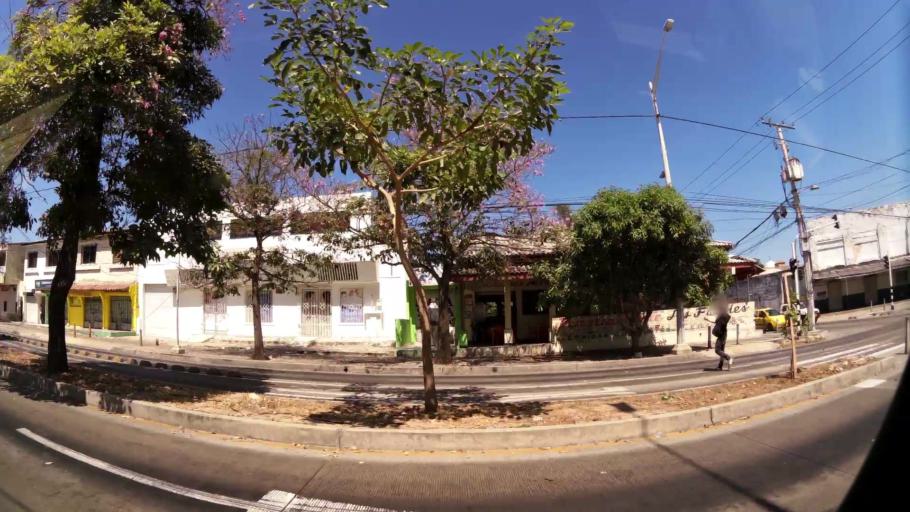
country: CO
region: Atlantico
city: Barranquilla
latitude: 10.9901
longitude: -74.7951
